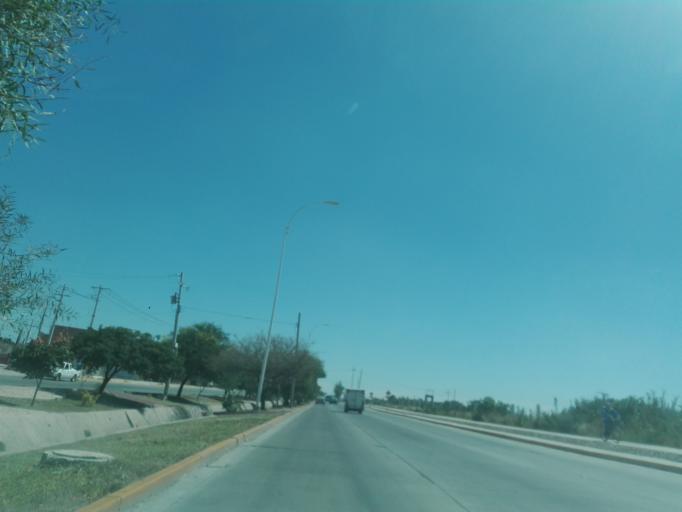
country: MX
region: Guanajuato
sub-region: Leon
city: San Jose de Duran (Los Troncoso)
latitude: 21.0713
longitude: -101.6434
